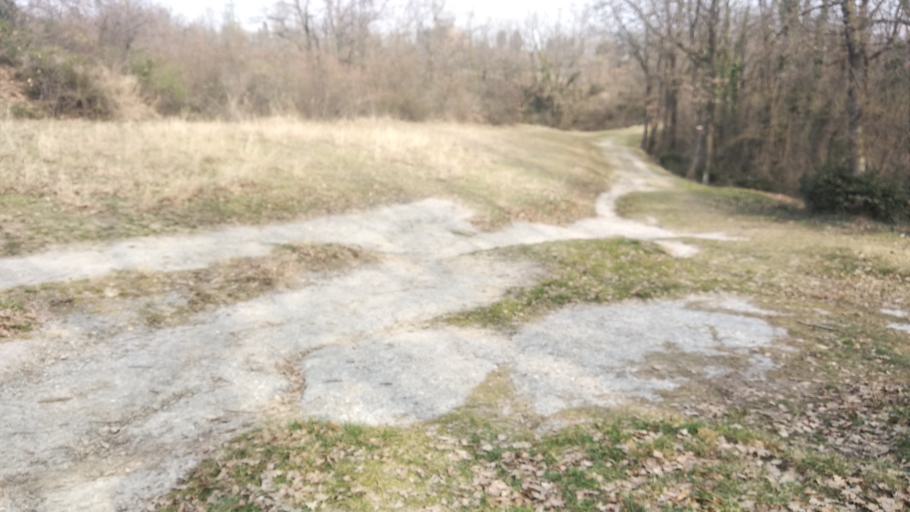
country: IT
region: Emilia-Romagna
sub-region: Provincia di Bologna
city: Ponticella
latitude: 44.4445
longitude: 11.3749
